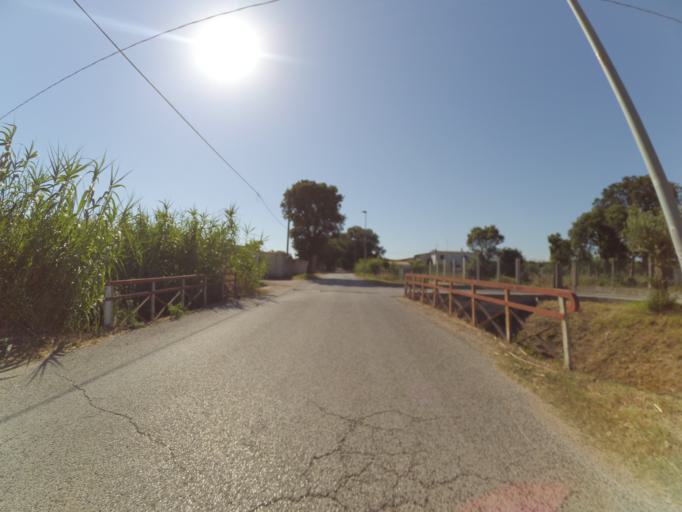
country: IT
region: Latium
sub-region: Provincia di Latina
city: San Felice Circeo
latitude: 41.2525
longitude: 13.0847
